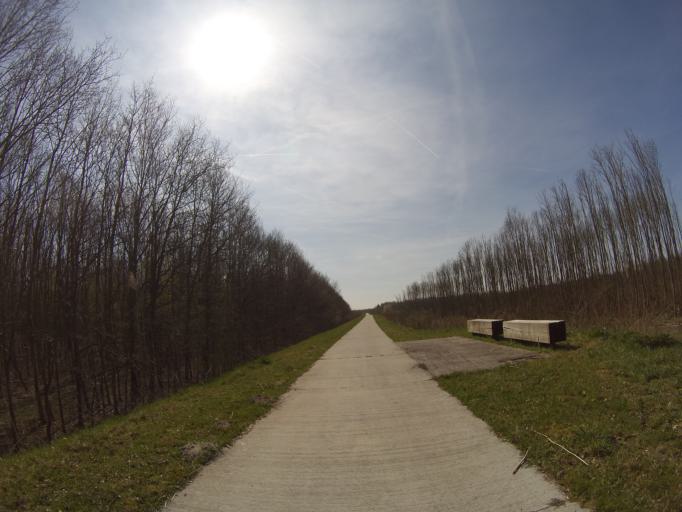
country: NL
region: Flevoland
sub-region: Gemeente Zeewolde
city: Zeewolde
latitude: 52.3126
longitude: 5.4695
